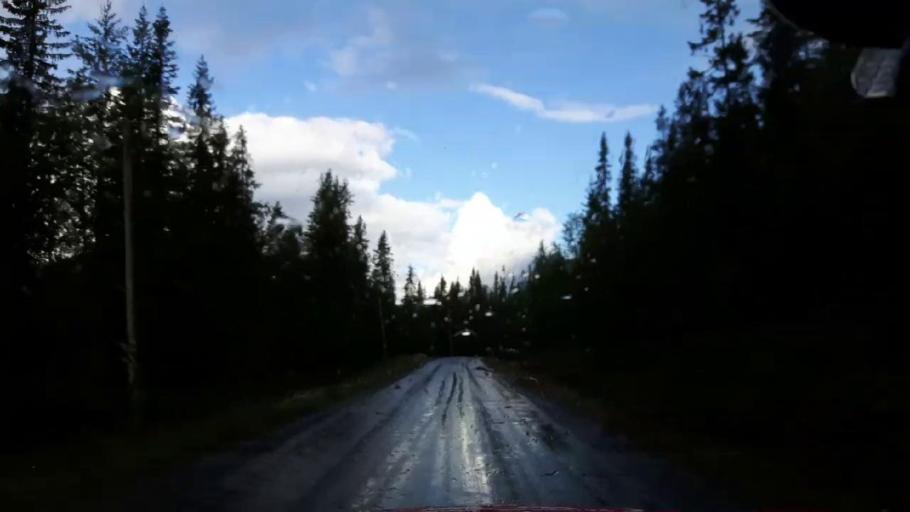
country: NO
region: Nordland
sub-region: Hattfjelldal
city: Hattfjelldal
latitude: 64.8660
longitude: 14.8884
